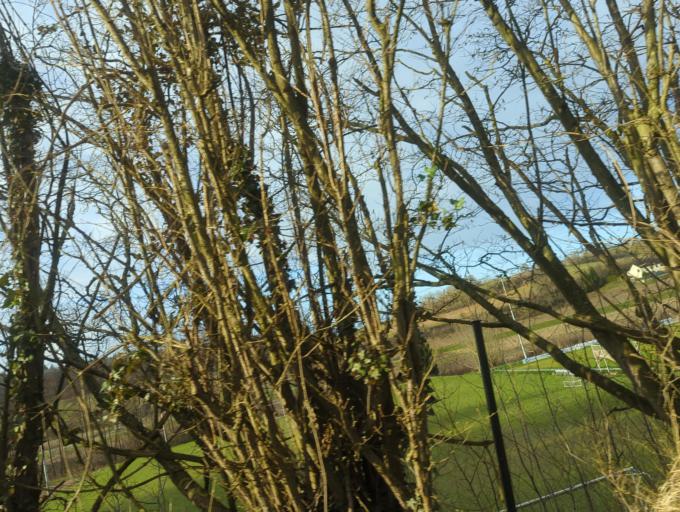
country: DE
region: Baden-Wuerttemberg
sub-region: Karlsruhe Region
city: Joehlingen
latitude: 49.0257
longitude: 8.5859
